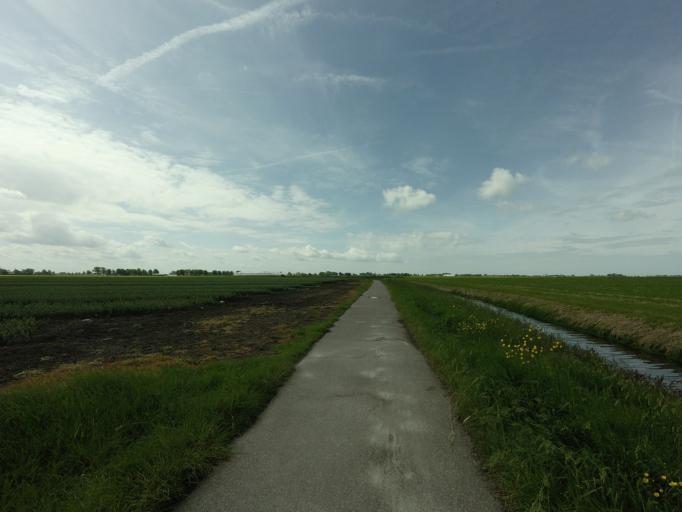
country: NL
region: North Holland
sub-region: Gemeente Opmeer
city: Opmeer
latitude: 52.6771
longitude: 5.0034
